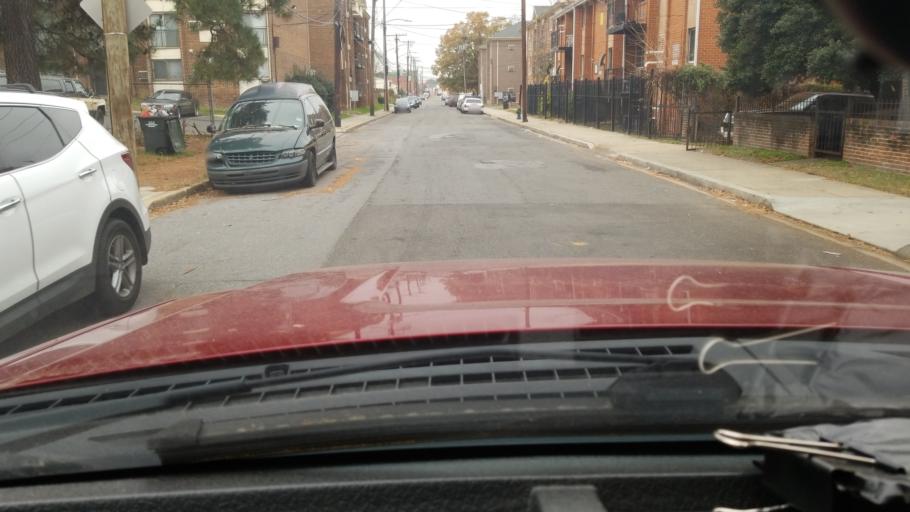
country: US
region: Maryland
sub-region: Prince George's County
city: Capitol Heights
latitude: 38.8817
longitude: -76.9246
